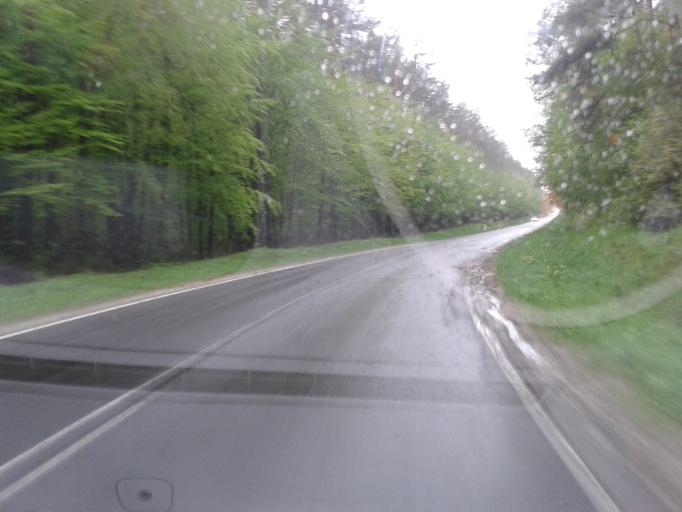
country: PL
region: Subcarpathian Voivodeship
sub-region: Powiat lubaczowski
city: Narol
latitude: 50.3195
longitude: 23.2677
